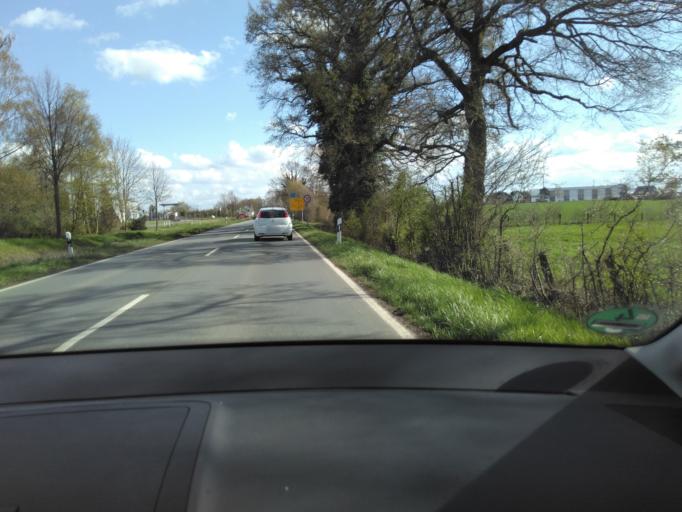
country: DE
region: North Rhine-Westphalia
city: Oelde
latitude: 51.7880
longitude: 8.1439
